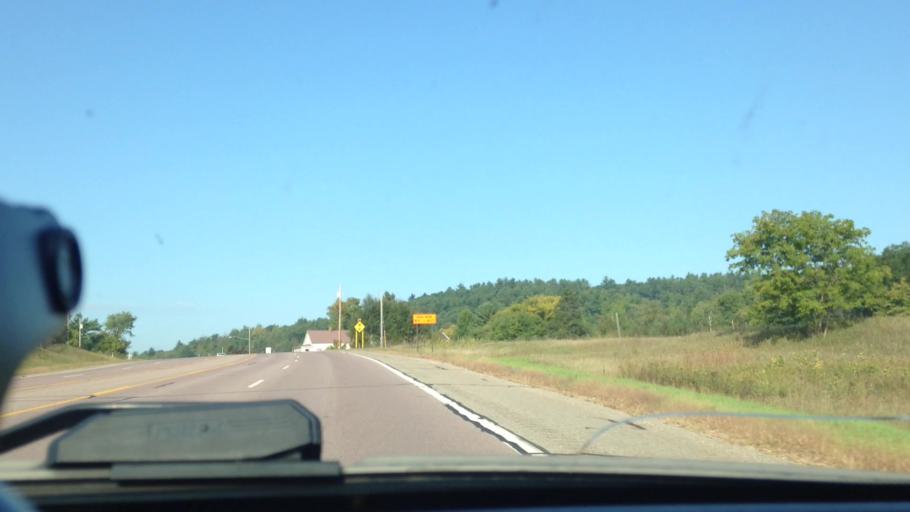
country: US
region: Michigan
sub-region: Dickinson County
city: Quinnesec
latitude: 45.8064
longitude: -87.9826
